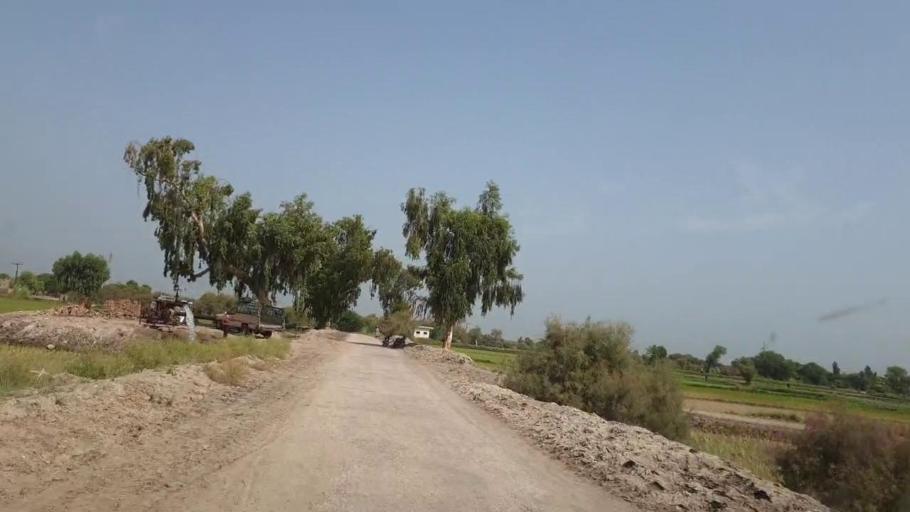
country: PK
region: Sindh
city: Lakhi
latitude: 27.8346
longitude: 68.6812
